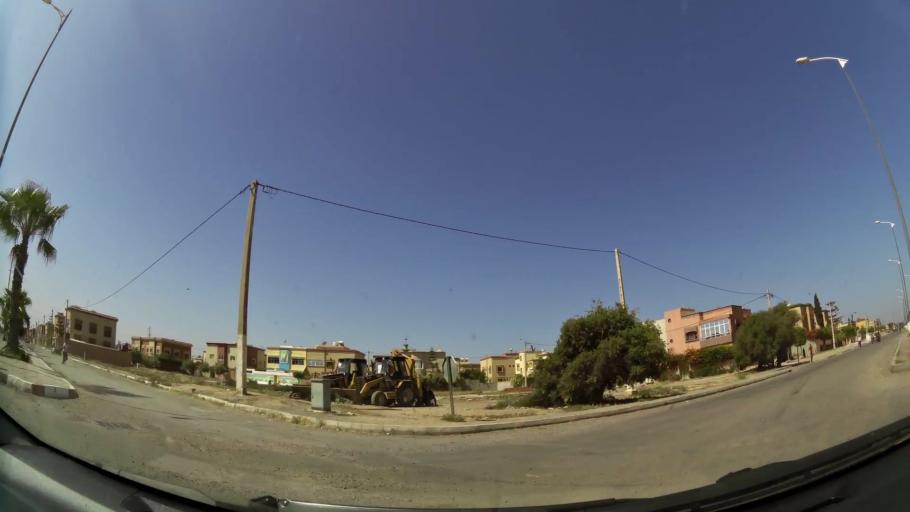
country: MA
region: Souss-Massa-Draa
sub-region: Inezgane-Ait Mellou
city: Inezgane
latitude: 30.3257
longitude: -9.5036
